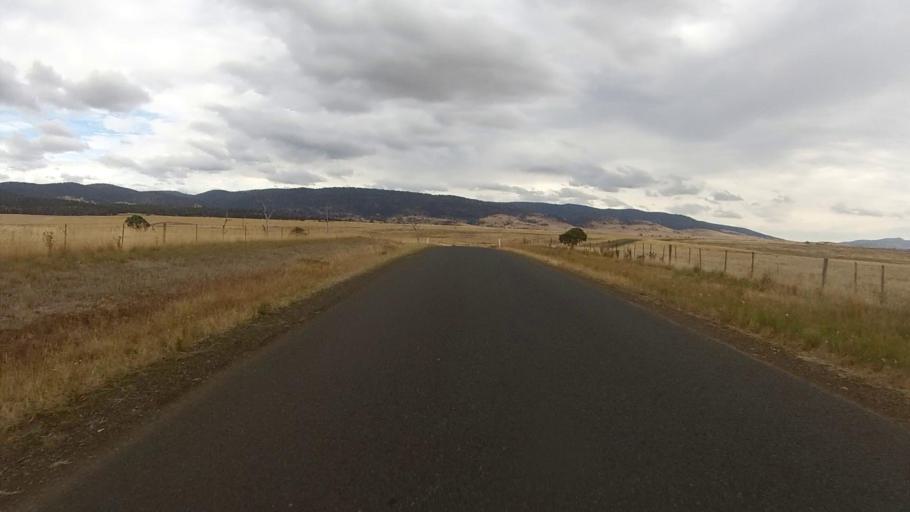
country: AU
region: Tasmania
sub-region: Northern Midlands
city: Evandale
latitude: -41.8271
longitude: 147.7906
